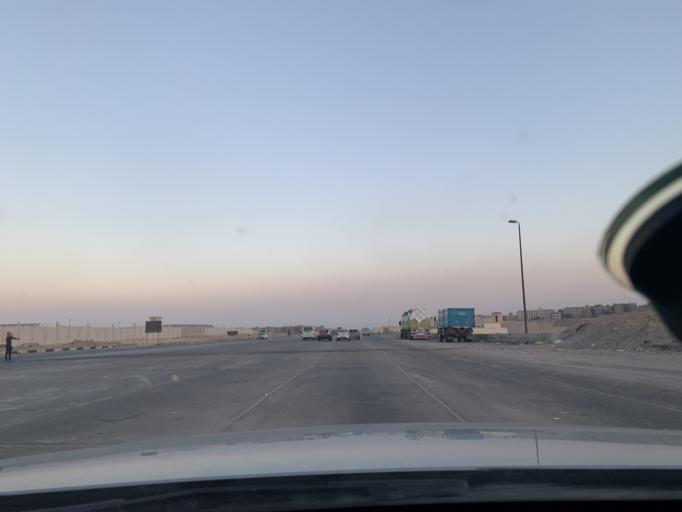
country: EG
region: Muhafazat al Qalyubiyah
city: Al Khankah
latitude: 30.1973
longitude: 31.4215
